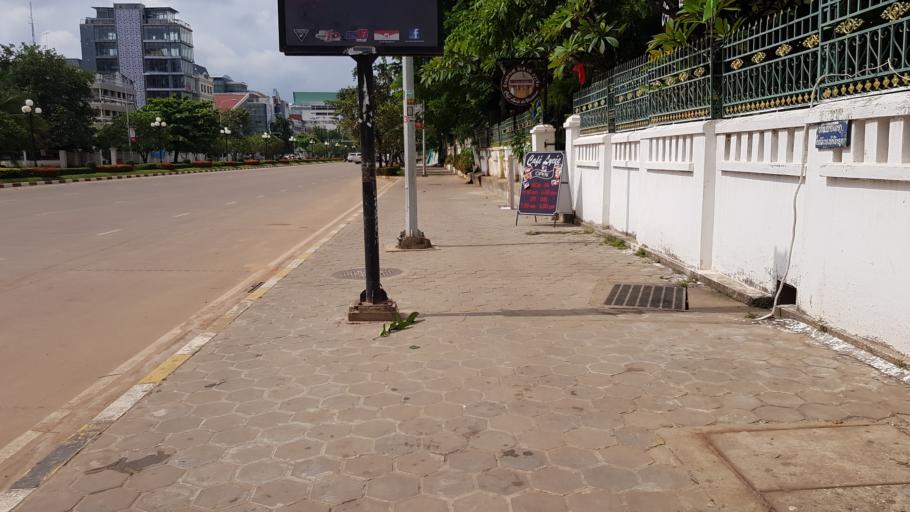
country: LA
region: Vientiane
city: Vientiane
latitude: 17.9694
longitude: 102.6170
